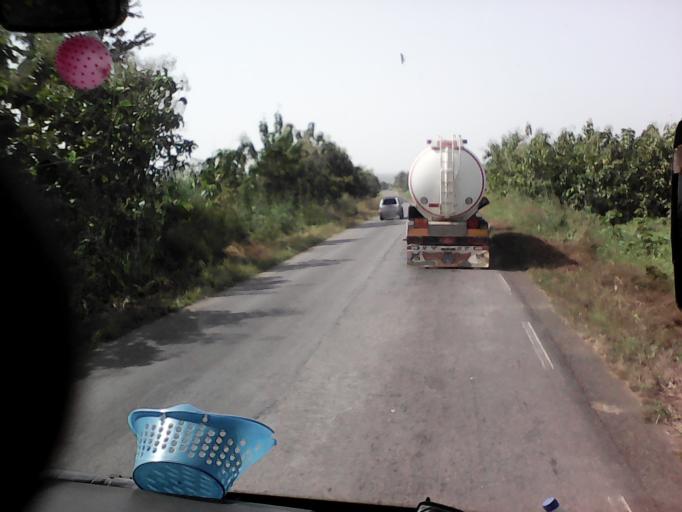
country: TG
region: Centrale
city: Sotouboua
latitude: 8.7635
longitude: 1.0597
